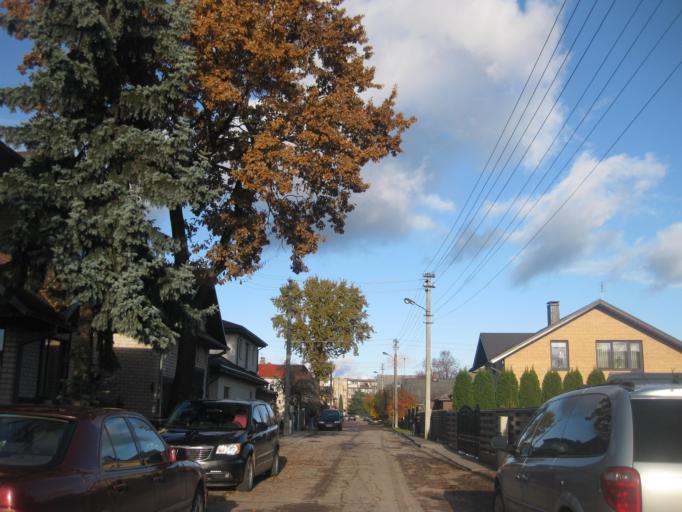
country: LT
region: Kauno apskritis
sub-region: Kaunas
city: Silainiai
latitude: 54.9171
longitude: 23.8928
